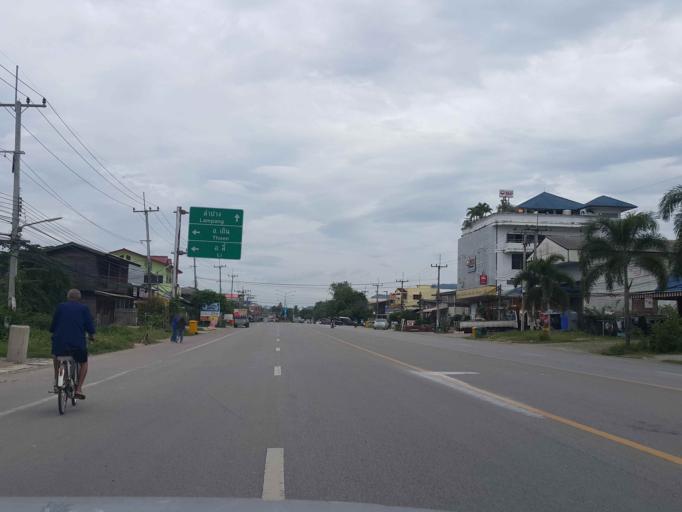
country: TH
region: Lampang
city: Thoen
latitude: 17.6374
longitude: 99.2354
